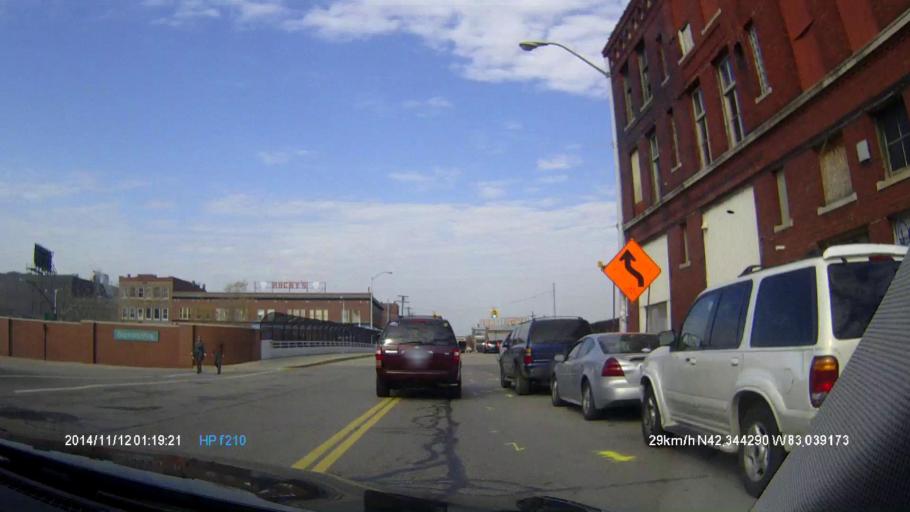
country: US
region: Michigan
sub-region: Wayne County
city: Detroit
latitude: 42.3444
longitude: -83.0392
